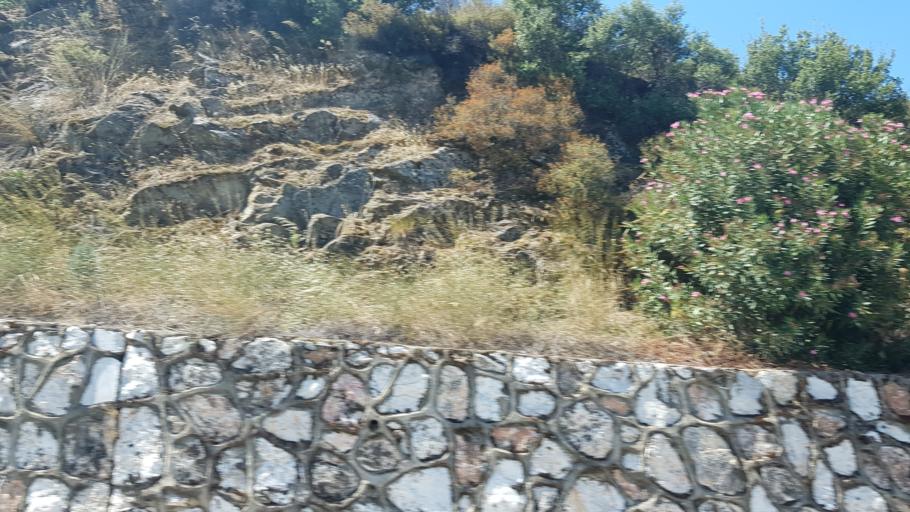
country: TR
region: Aydin
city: Akcaova
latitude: 37.5109
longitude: 28.0990
